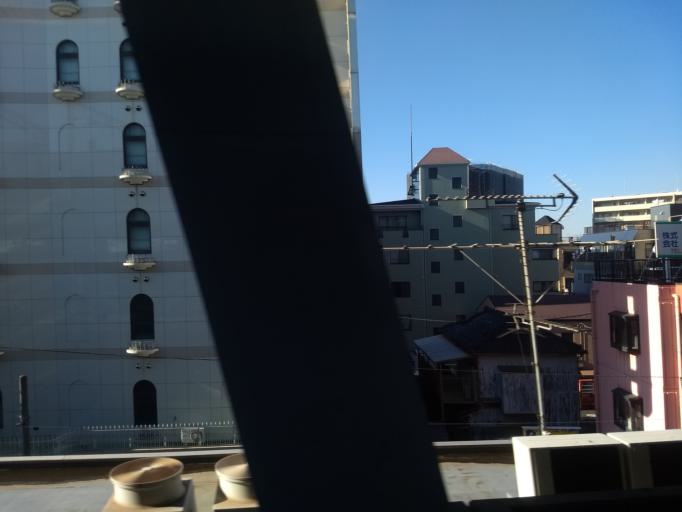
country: JP
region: Chiba
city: Matsudo
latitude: 35.7466
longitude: 139.8567
